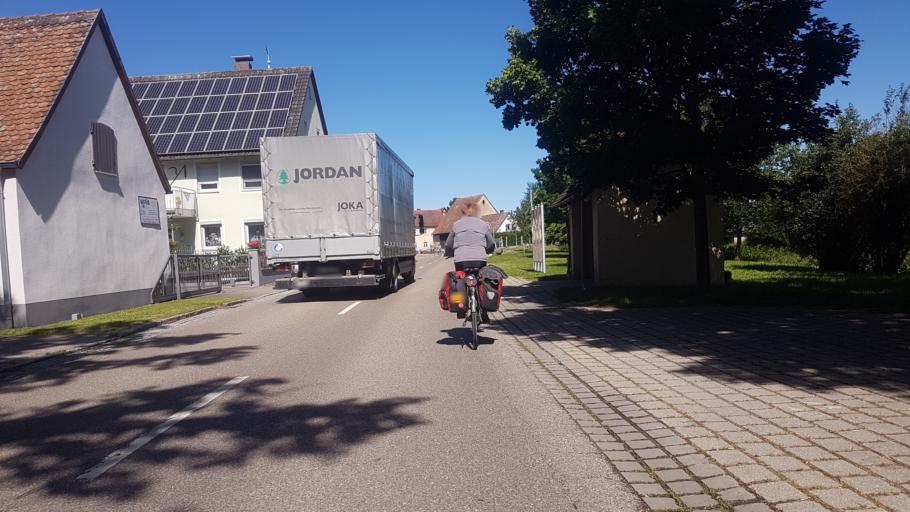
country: DE
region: Bavaria
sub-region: Regierungsbezirk Mittelfranken
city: Burgoberbach
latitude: 49.2051
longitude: 10.5495
